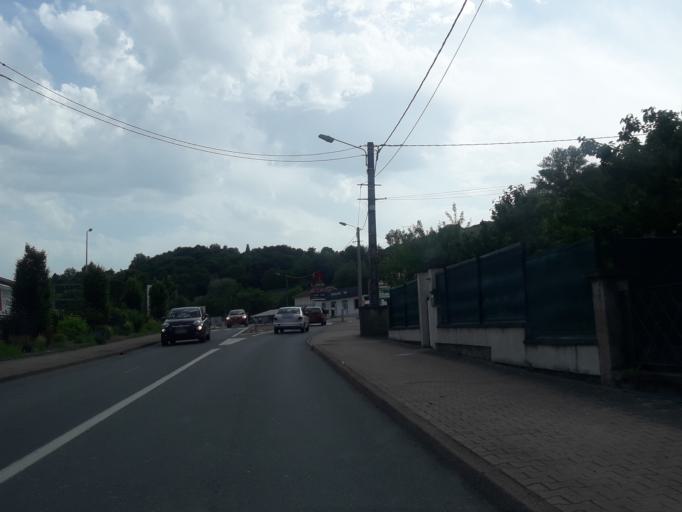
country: FR
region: Rhone-Alpes
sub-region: Departement du Rhone
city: Sain-Bel
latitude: 45.8260
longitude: 4.6069
